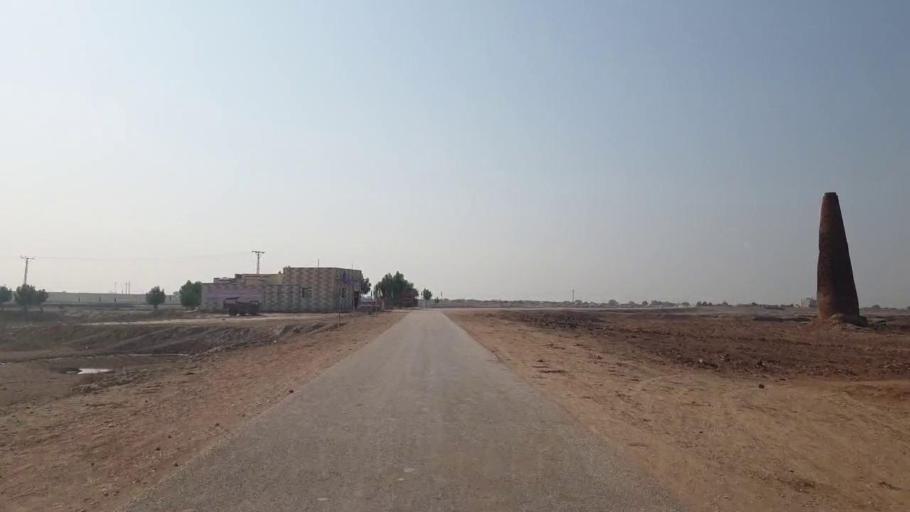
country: PK
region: Sindh
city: Sehwan
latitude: 26.4333
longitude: 67.8442
